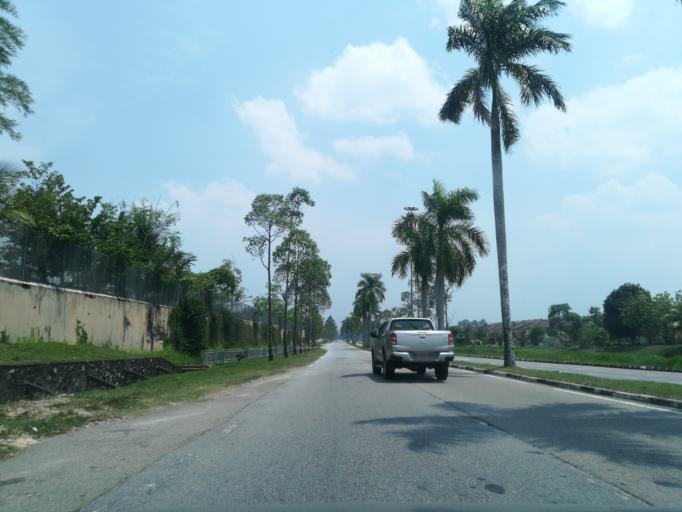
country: MY
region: Kedah
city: Kulim
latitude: 5.3999
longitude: 100.5758
